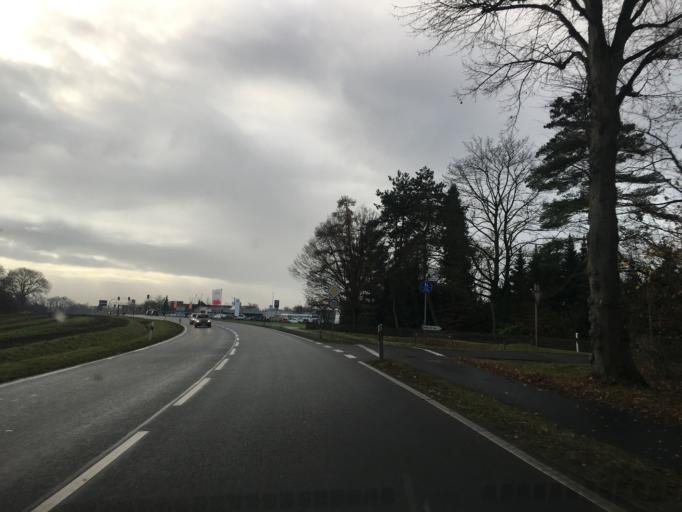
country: DE
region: North Rhine-Westphalia
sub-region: Regierungsbezirk Munster
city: Senden
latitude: 51.8491
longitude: 7.4889
